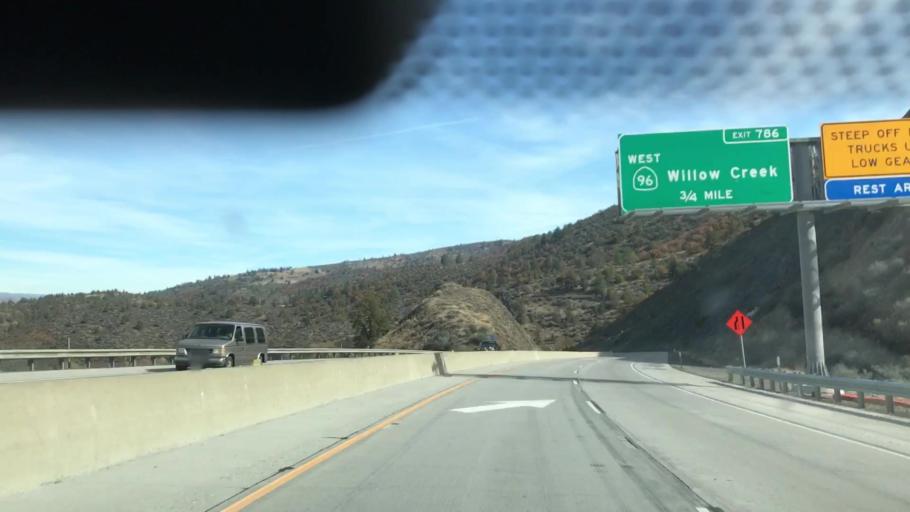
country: US
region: California
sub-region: Siskiyou County
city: Yreka
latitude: 41.8437
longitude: -122.5740
